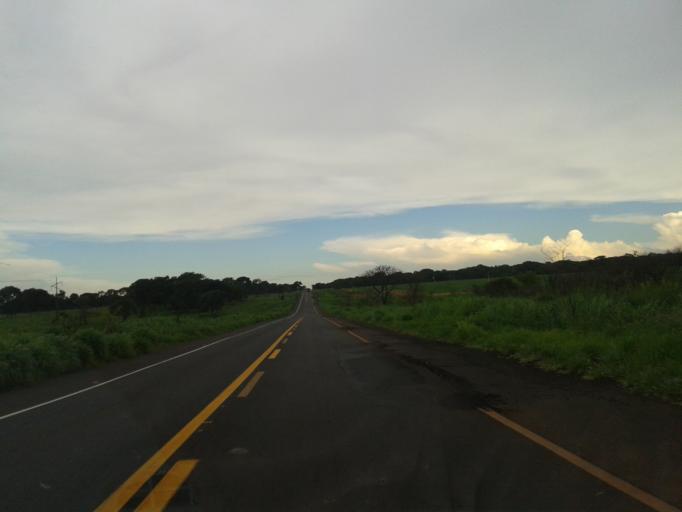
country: BR
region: Minas Gerais
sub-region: Santa Vitoria
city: Santa Vitoria
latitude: -18.9209
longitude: -50.2479
